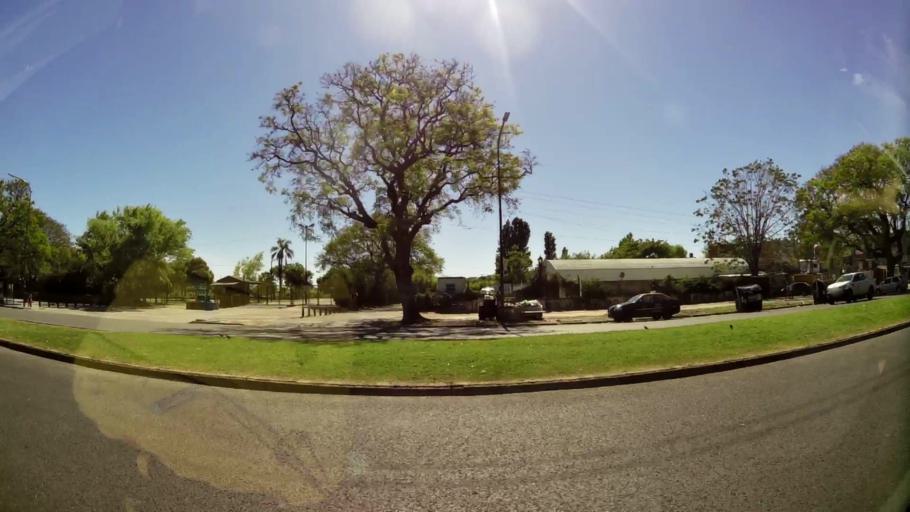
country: AR
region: Buenos Aires F.D.
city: Buenos Aires
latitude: -34.6188
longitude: -58.3559
